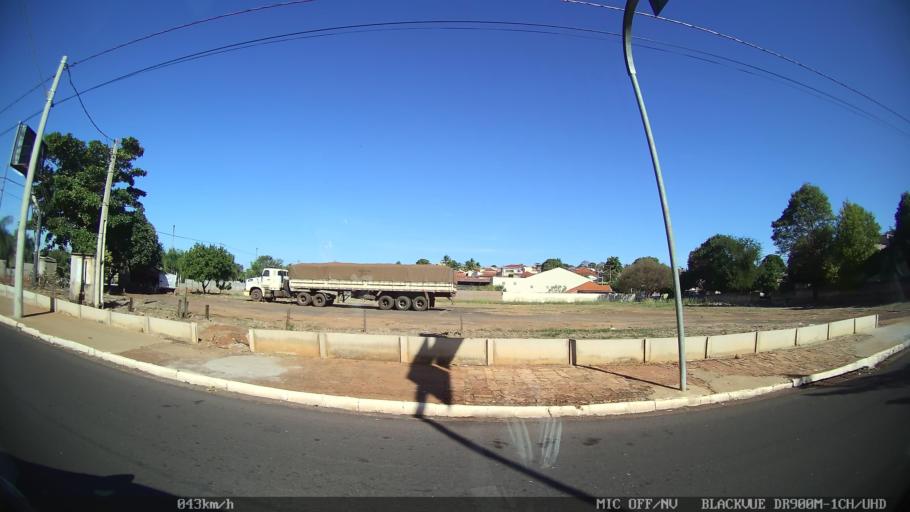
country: BR
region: Sao Paulo
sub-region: Olimpia
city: Olimpia
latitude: -20.7408
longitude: -48.9107
